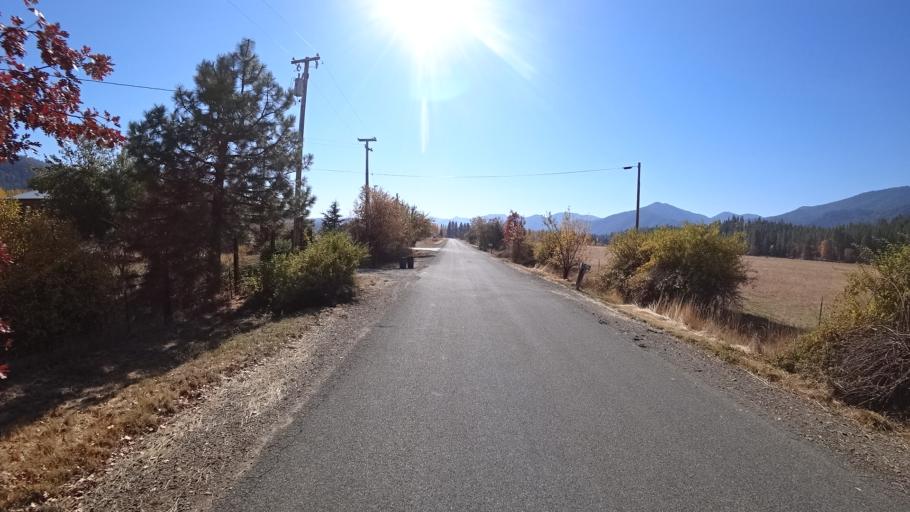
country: US
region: California
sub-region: Siskiyou County
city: Yreka
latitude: 41.6170
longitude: -122.9704
